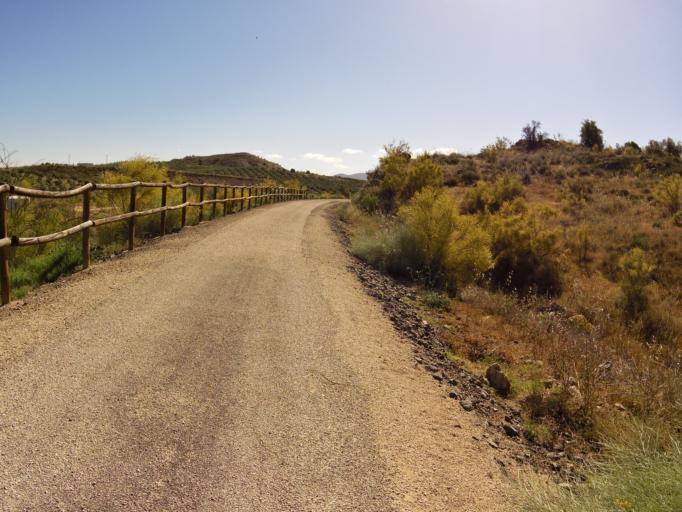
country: ES
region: Andalusia
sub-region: Provincia de Jaen
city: Alcaudete
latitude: 37.6054
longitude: -4.1566
